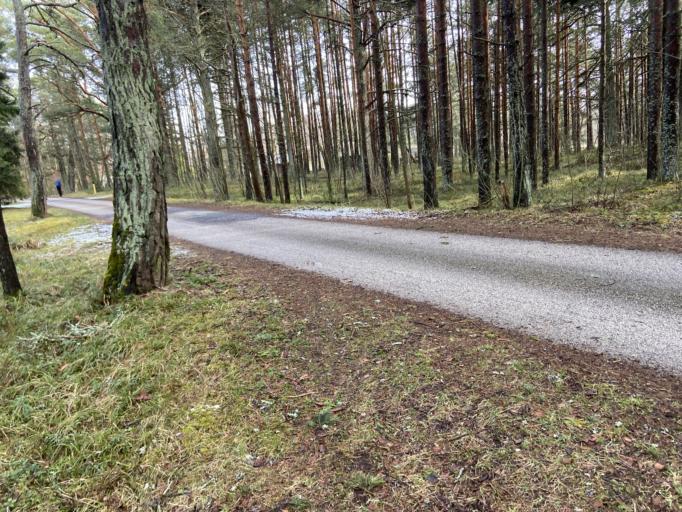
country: EE
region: Harju
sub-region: Loksa linn
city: Loksa
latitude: 59.6556
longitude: 25.6812
